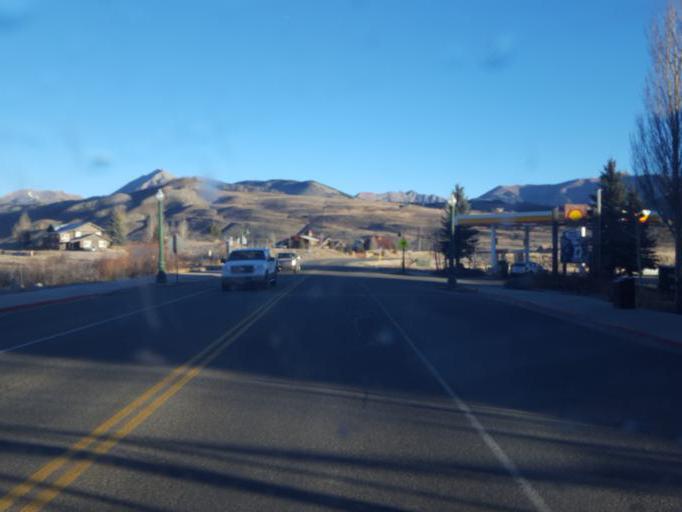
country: US
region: Colorado
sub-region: Gunnison County
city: Crested Butte
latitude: 38.8725
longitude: -106.9809
